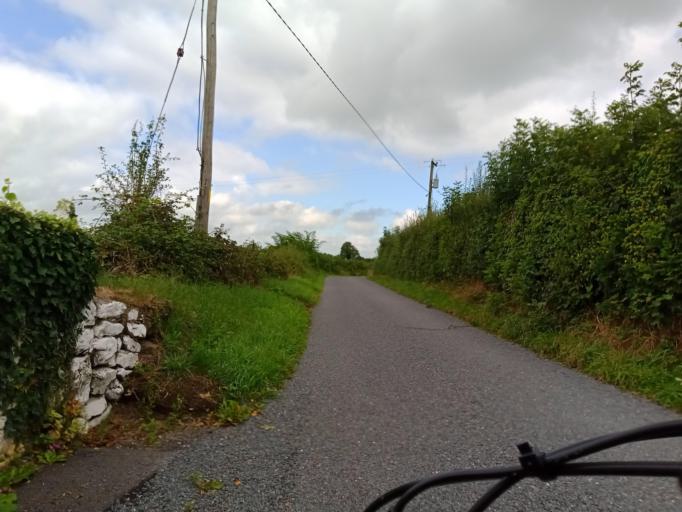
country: IE
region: Leinster
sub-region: Kilkenny
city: Callan
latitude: 52.5321
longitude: -7.2877
